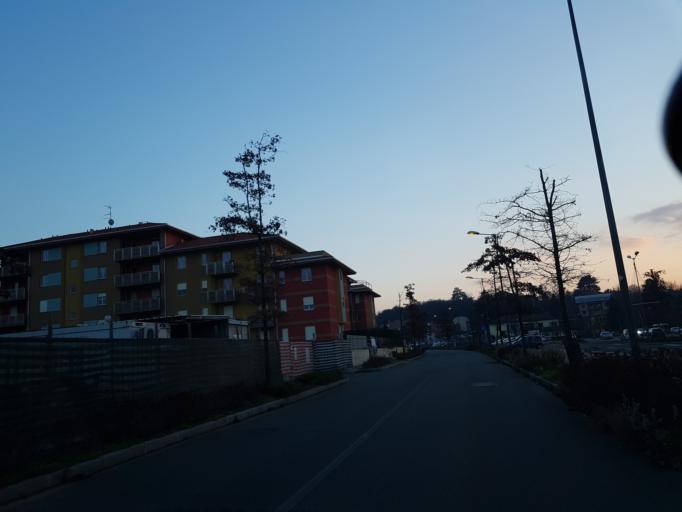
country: IT
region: Piedmont
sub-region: Provincia di Alessandria
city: Novi Ligure
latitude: 44.7670
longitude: 8.7744
